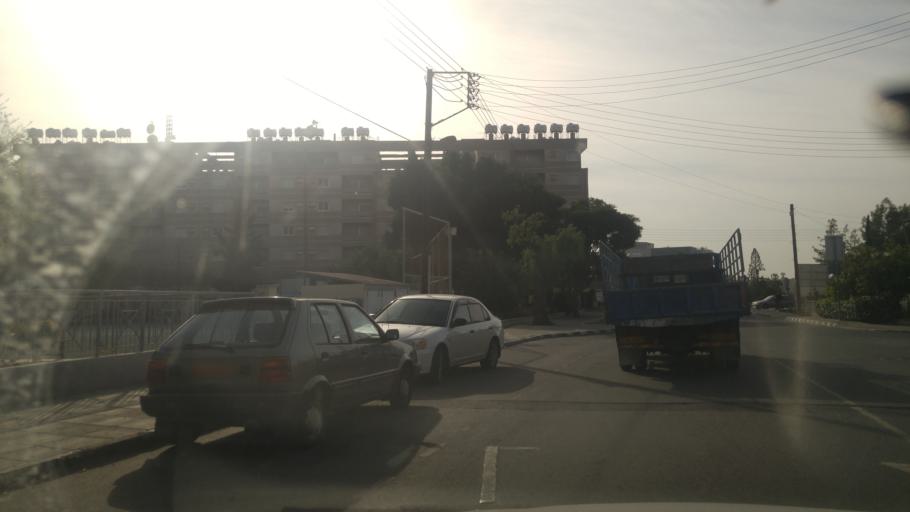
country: CY
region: Limassol
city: Limassol
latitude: 34.6589
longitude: 33.0015
